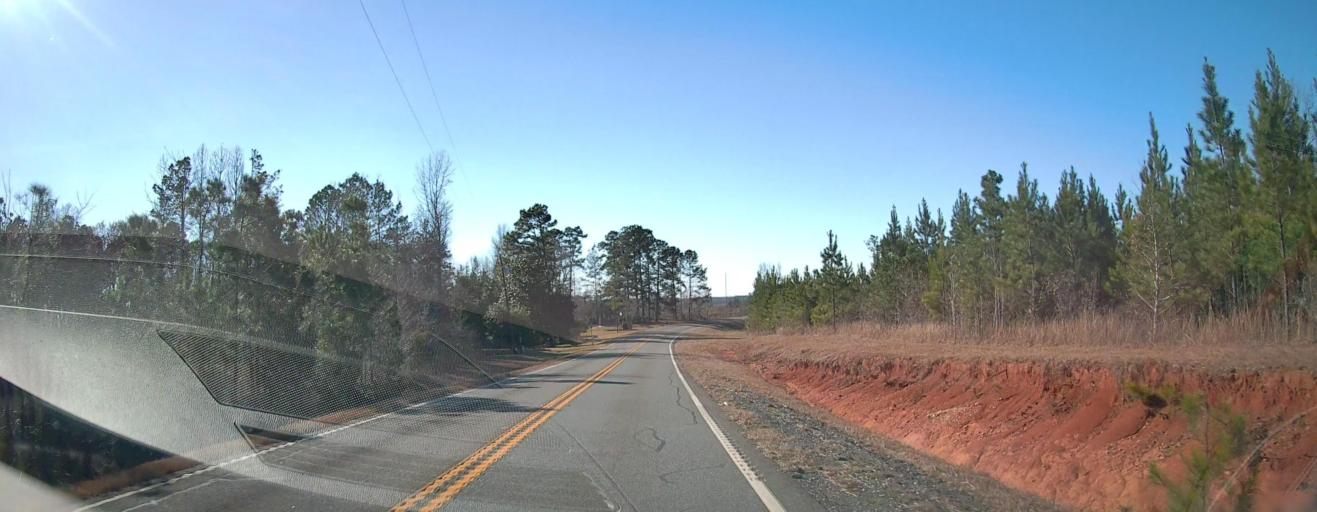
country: US
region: Georgia
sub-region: Talbot County
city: Talbotton
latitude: 32.6514
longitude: -84.4536
